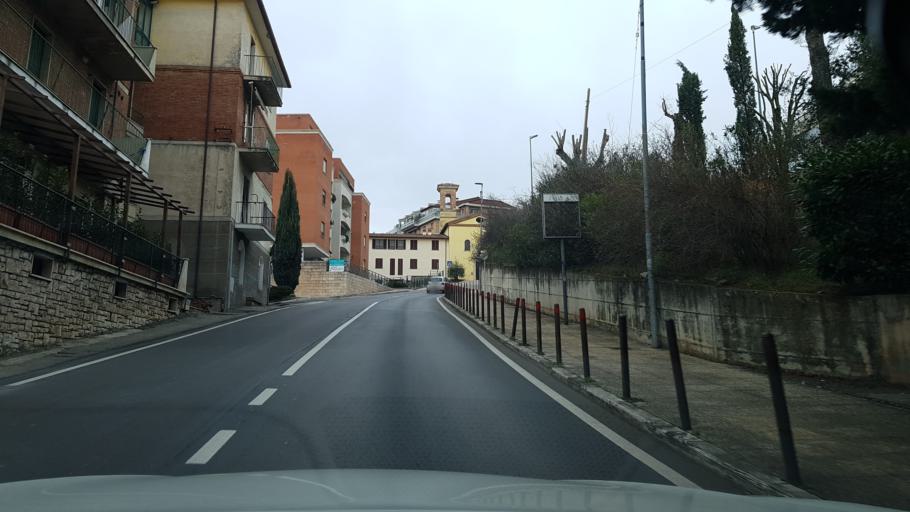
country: IT
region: Umbria
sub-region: Provincia di Perugia
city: Perugia
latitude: 43.1187
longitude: 12.3648
